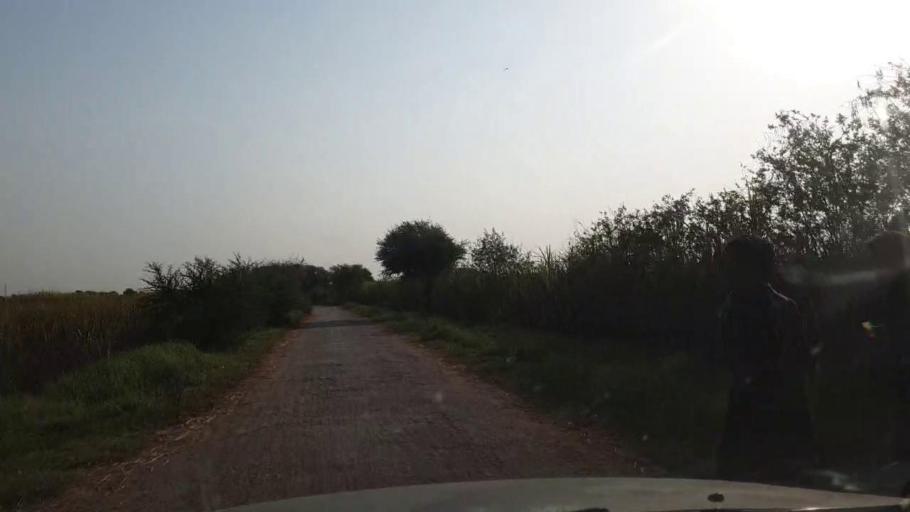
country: PK
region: Sindh
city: Bulri
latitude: 24.9468
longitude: 68.3427
